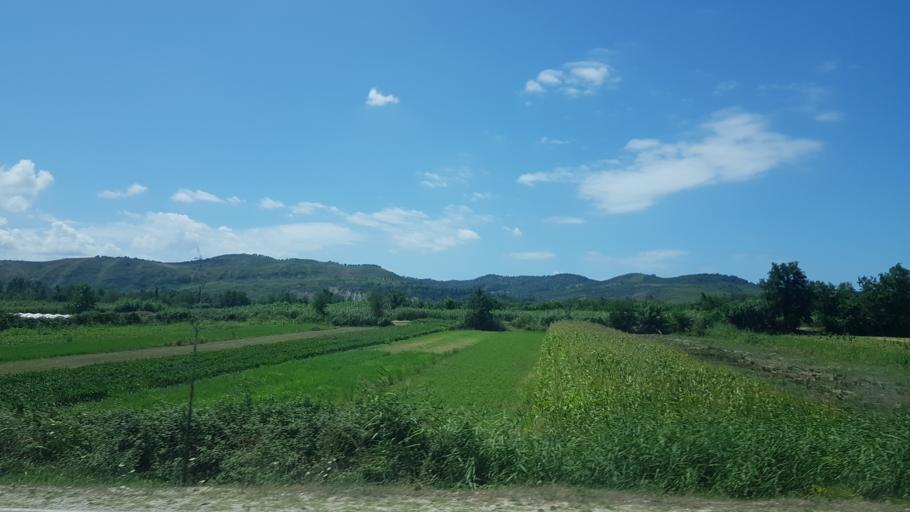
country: AL
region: Fier
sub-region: Rrethi i Fierit
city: Frakulla e Madhe
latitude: 40.6104
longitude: 19.5278
